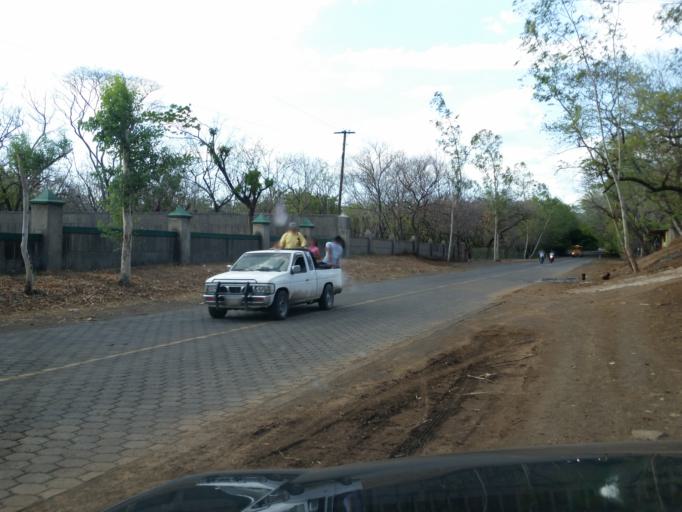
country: NI
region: Managua
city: Carlos Fonseca Amador
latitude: 12.0631
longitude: -86.5034
